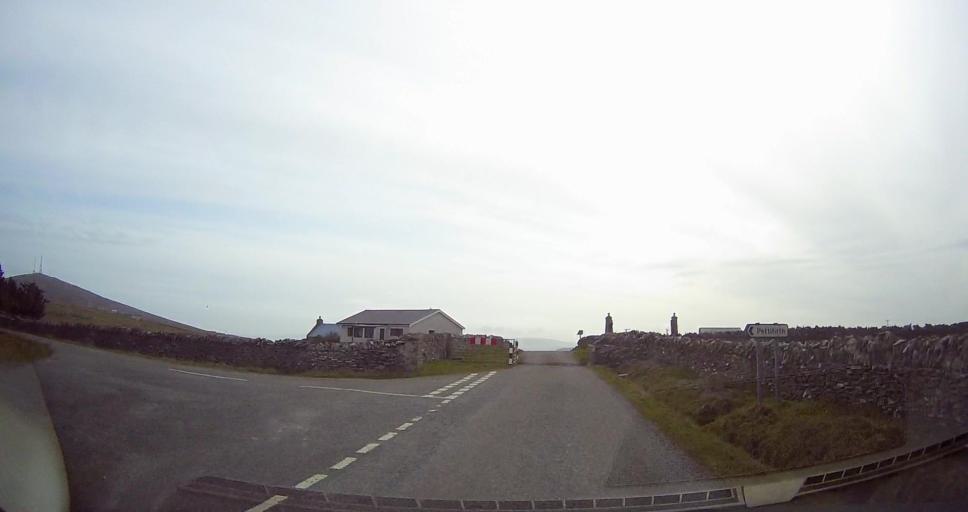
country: GB
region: Scotland
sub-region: Shetland Islands
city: Shetland
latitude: 60.1530
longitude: -1.0948
